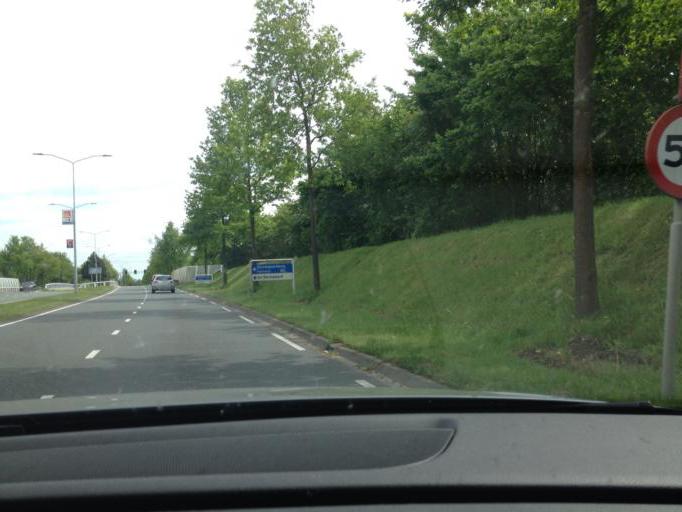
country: NL
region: Flevoland
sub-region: Gemeente Almere
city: Almere Stad
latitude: 52.3735
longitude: 5.2357
